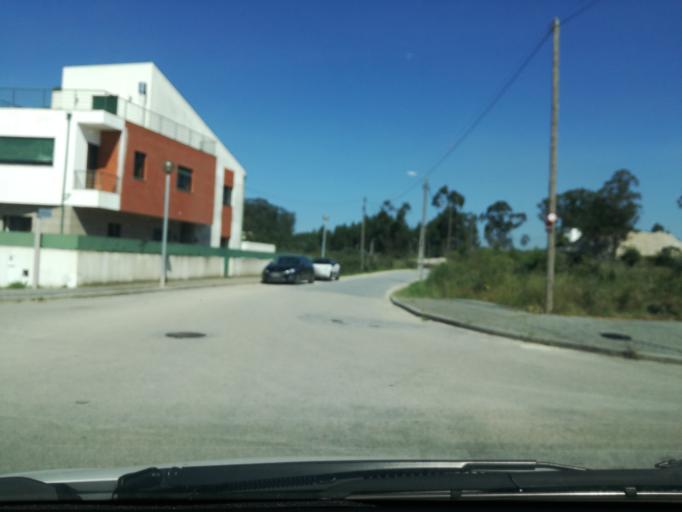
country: PT
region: Porto
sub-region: Maia
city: Nogueira
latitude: 41.2478
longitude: -8.5989
